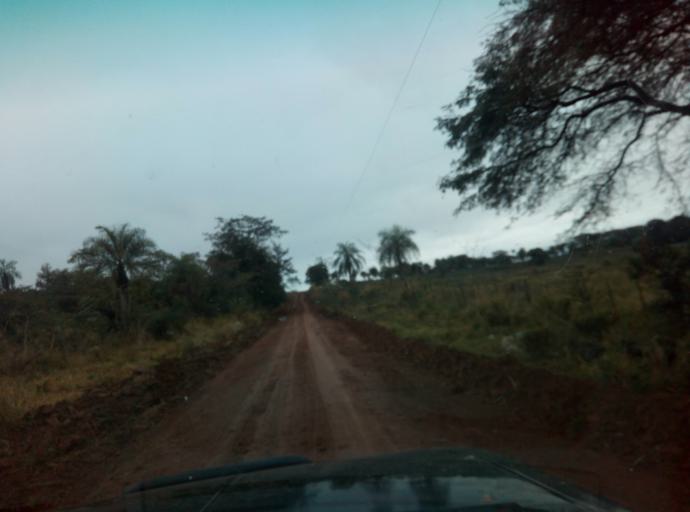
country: PY
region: Caaguazu
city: Carayao
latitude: -25.1903
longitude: -56.3727
